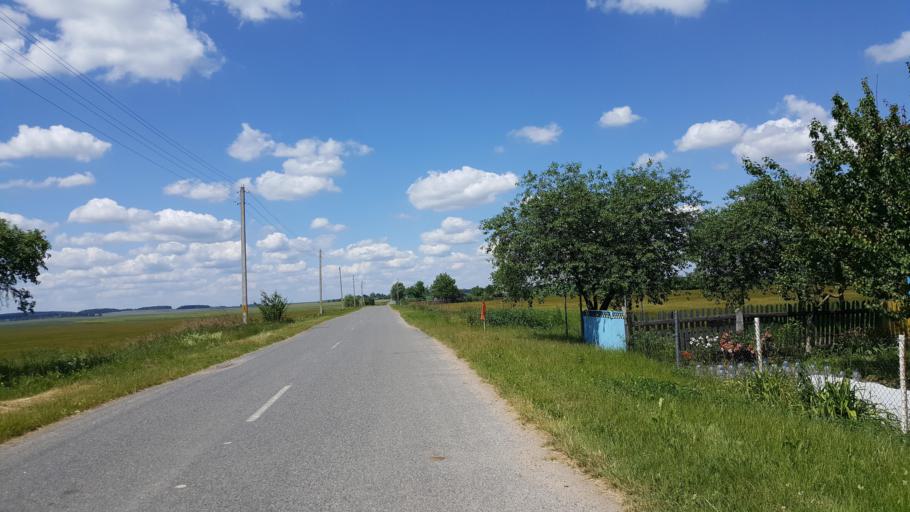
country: BY
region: Brest
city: Vysokaye
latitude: 52.4445
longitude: 23.5407
